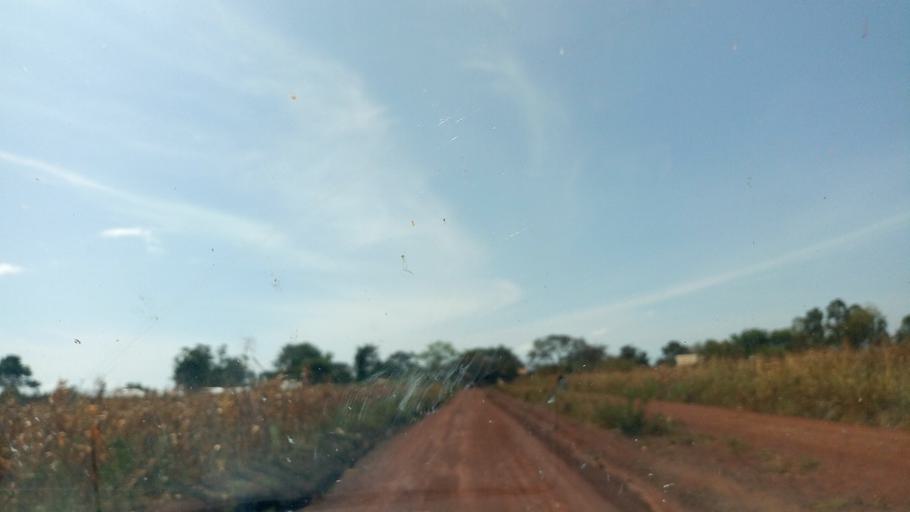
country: UG
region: Western Region
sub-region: Kiryandongo District
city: Kiryandongo
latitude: 1.9461
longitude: 32.1576
